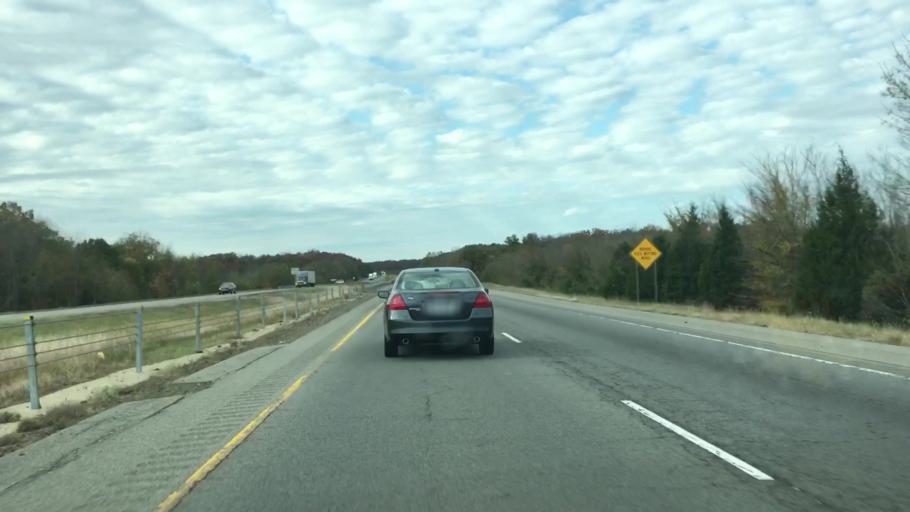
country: US
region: Arkansas
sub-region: Faulkner County
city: Conway
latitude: 35.1286
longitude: -92.5128
